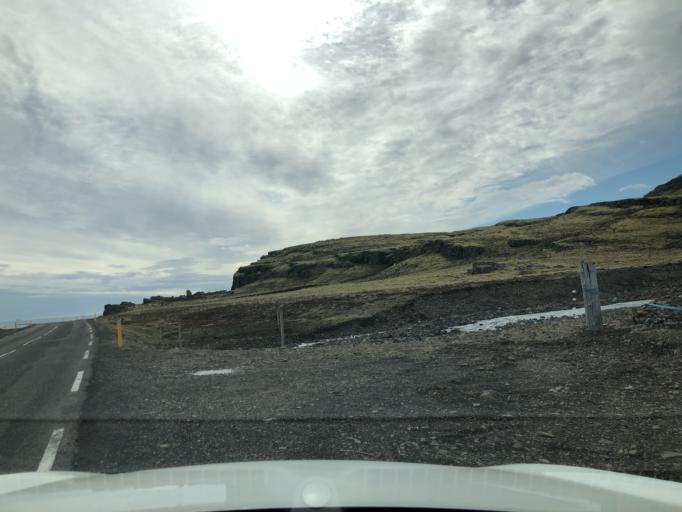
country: IS
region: East
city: Eskifjoerdur
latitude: 64.7605
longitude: -14.0428
